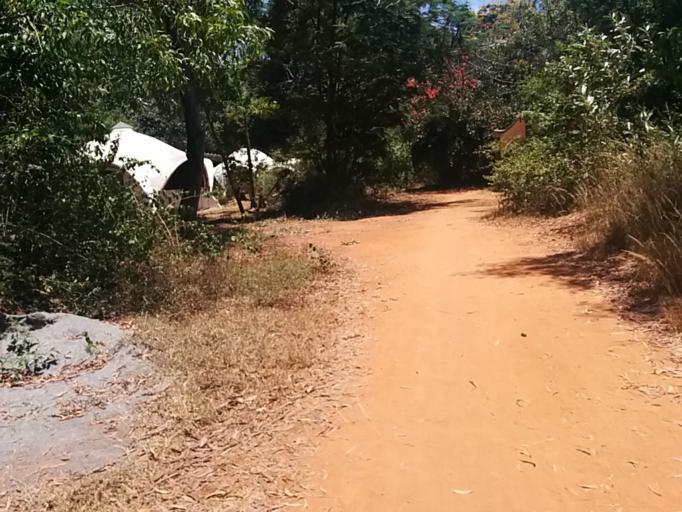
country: IN
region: Tamil Nadu
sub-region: Villupuram
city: Auroville
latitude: 12.0098
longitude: 79.8160
